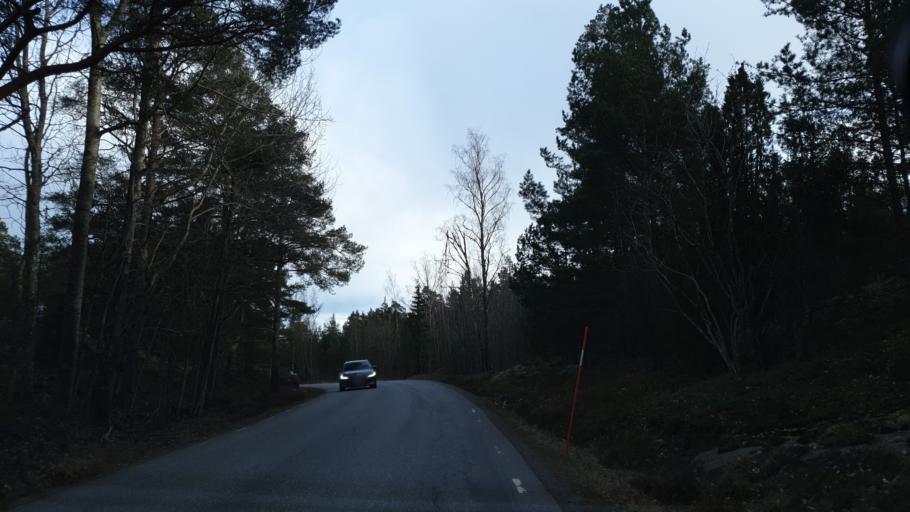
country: SE
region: Stockholm
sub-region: Varmdo Kommun
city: Holo
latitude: 59.3557
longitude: 18.7001
